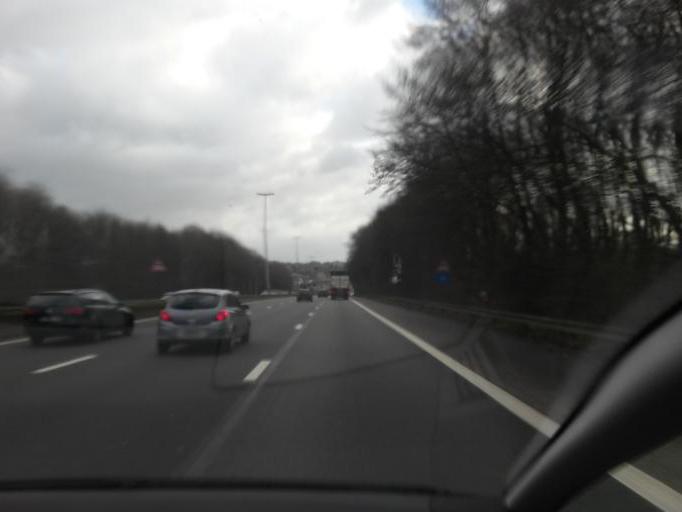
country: BE
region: Wallonia
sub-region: Province du Brabant Wallon
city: Wavre
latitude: 50.7142
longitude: 4.5946
